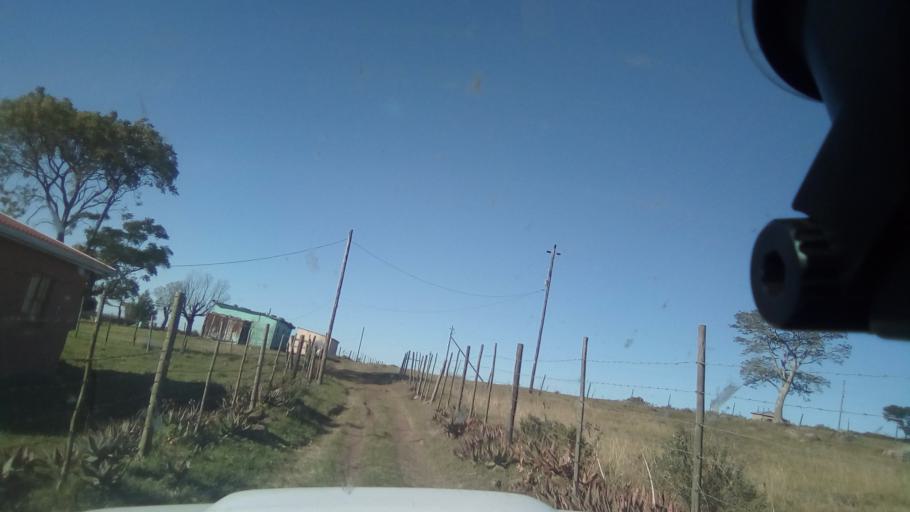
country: ZA
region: Eastern Cape
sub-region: Buffalo City Metropolitan Municipality
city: Bhisho
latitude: -32.9463
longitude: 27.2922
